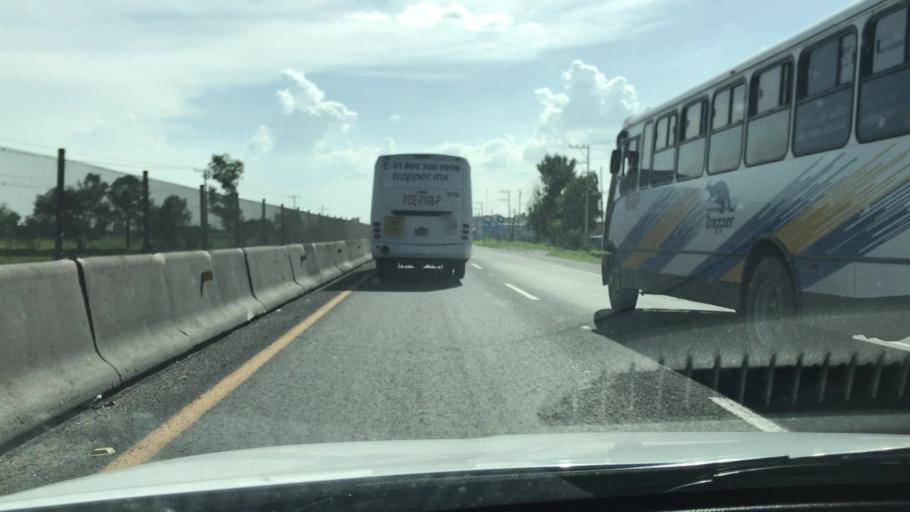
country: MX
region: Guanajuato
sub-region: Villagran
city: El Chinaco (El Pujido)
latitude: 20.5139
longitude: -100.9152
